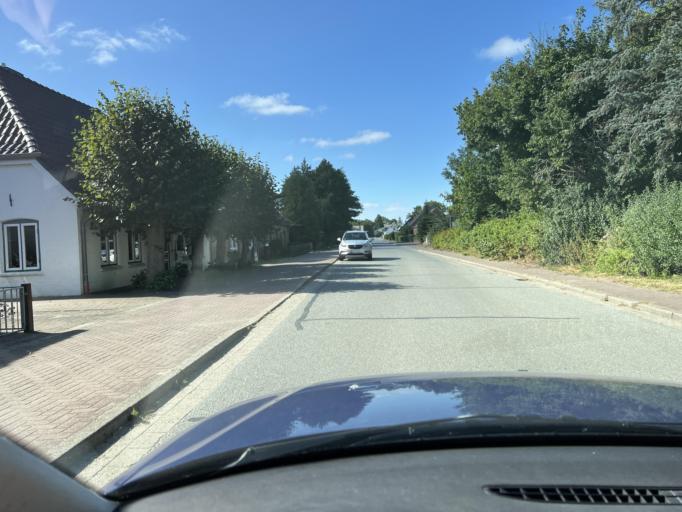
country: DE
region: Schleswig-Holstein
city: Norddeich
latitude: 54.2165
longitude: 8.9041
